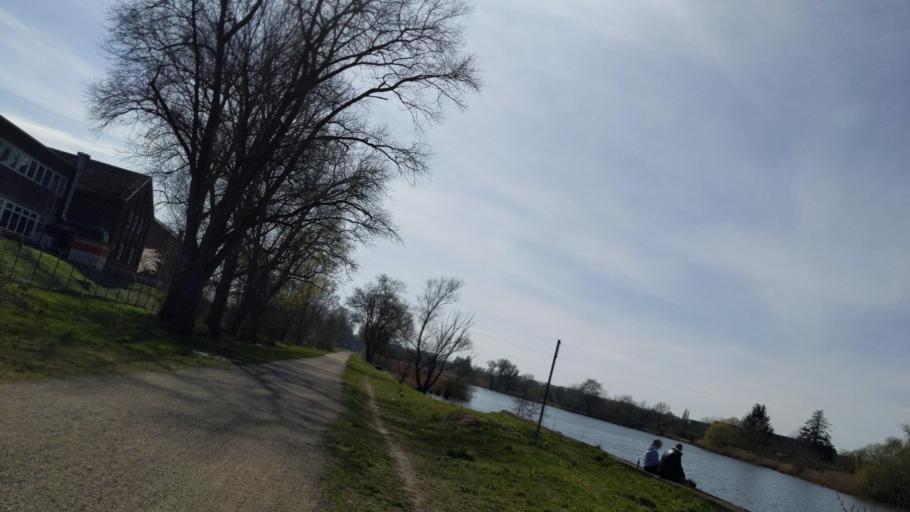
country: DE
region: Schleswig-Holstein
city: Luebeck
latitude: 53.8508
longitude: 10.6718
